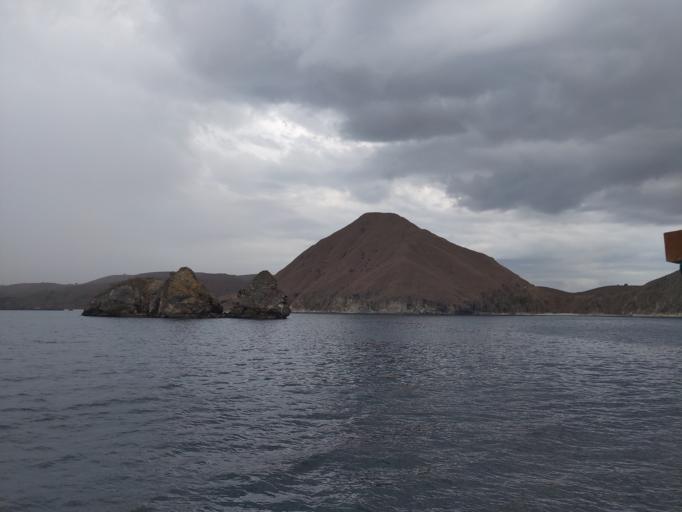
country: ID
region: East Nusa Tenggara
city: Komodo
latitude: -8.6674
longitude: 119.5941
